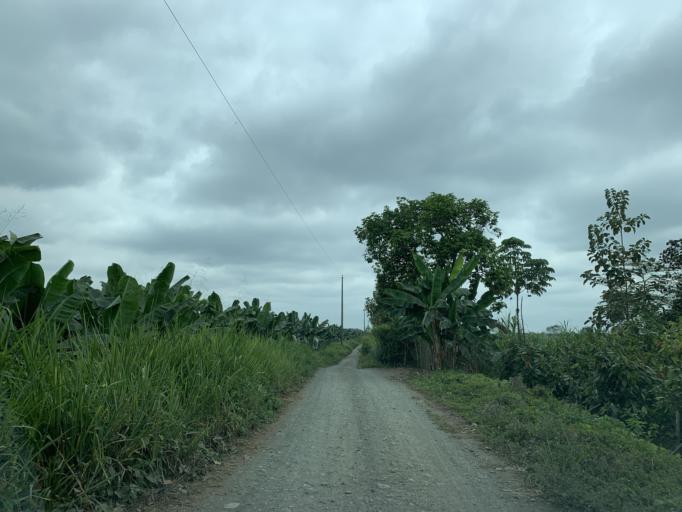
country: EC
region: Guayas
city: Coronel Marcelino Mariduena
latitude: -2.3403
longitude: -79.4573
